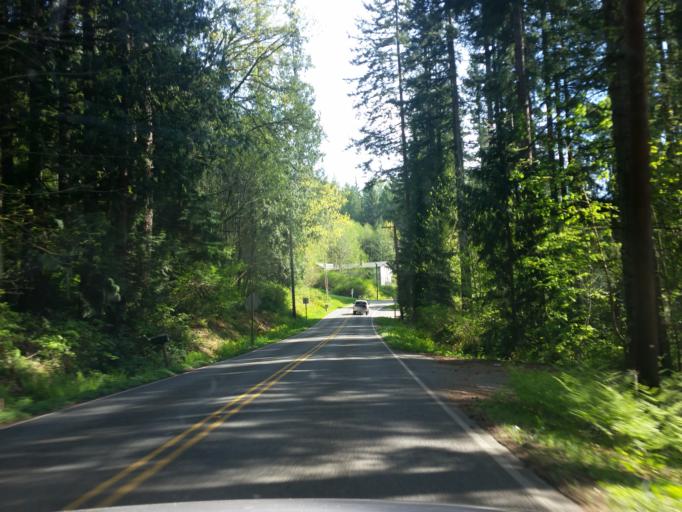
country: US
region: Washington
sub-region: Snohomish County
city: Woods Creek
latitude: 47.9804
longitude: -121.9141
